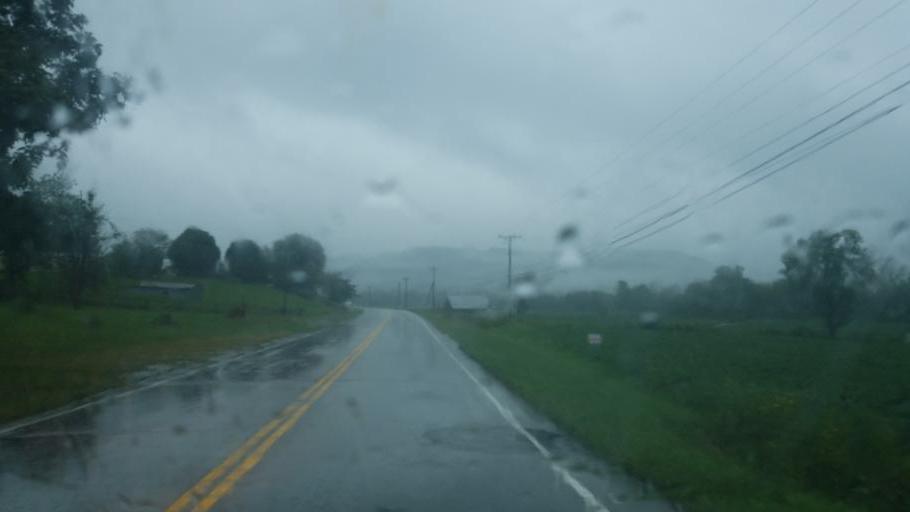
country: US
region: Kentucky
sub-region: Fleming County
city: Flemingsburg
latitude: 38.3183
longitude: -83.5764
